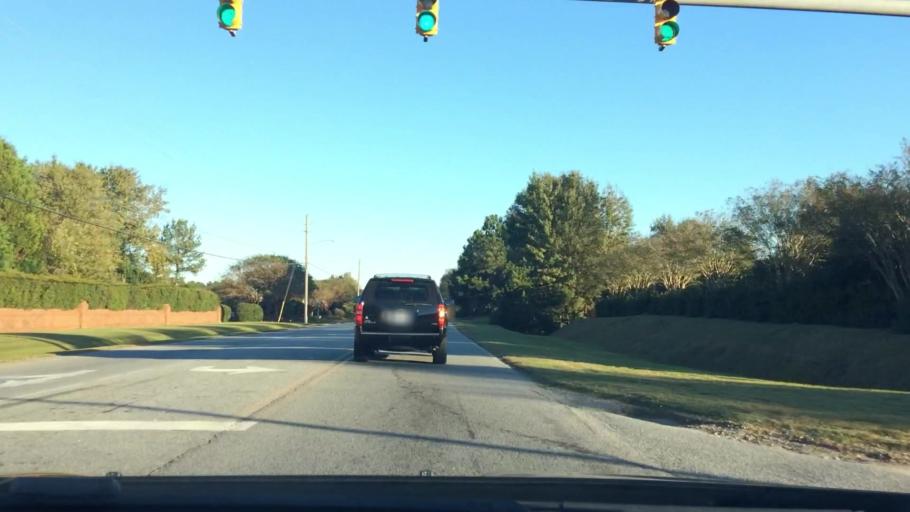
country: US
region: North Carolina
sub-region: Pitt County
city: Summerfield
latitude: 35.5563
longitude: -77.3856
